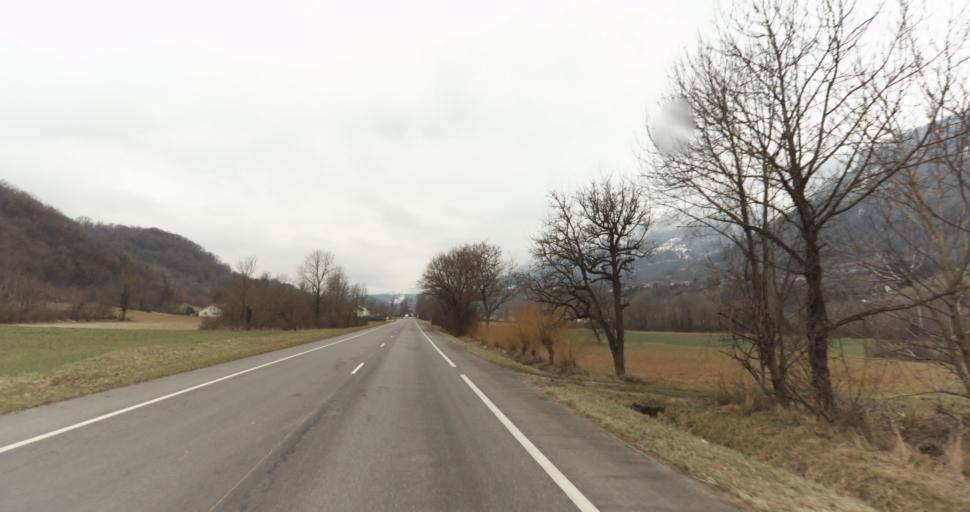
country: FR
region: Rhone-Alpes
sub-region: Departement de l'Isere
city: Vif
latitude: 45.0362
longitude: 5.6588
